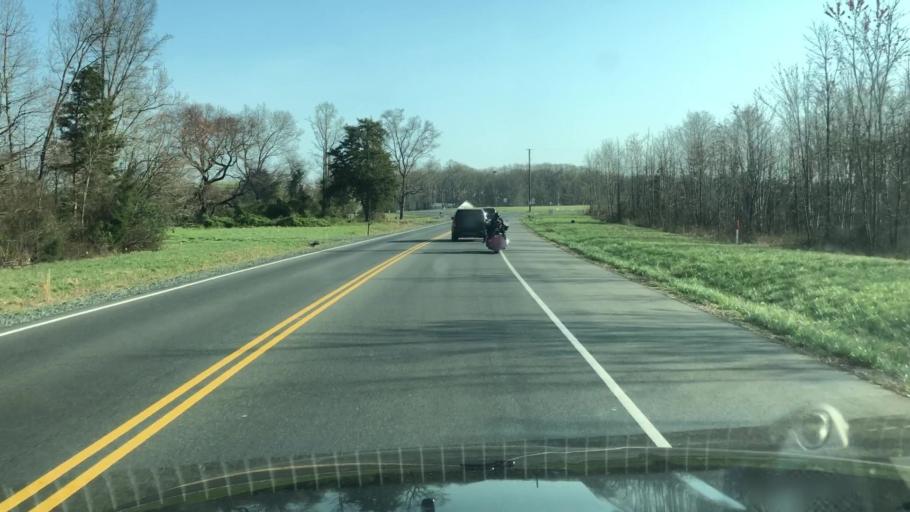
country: US
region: Virginia
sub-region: Stafford County
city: Falmouth
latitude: 38.3874
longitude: -77.5409
